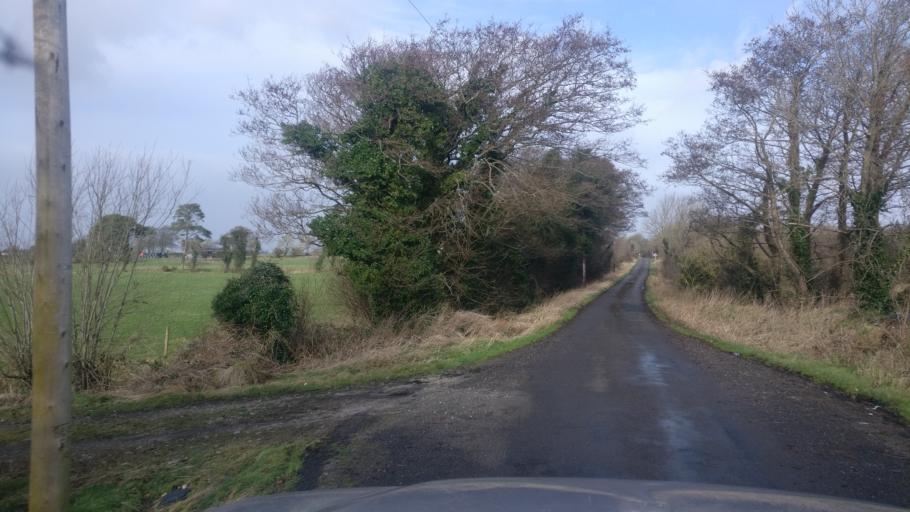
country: IE
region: Connaught
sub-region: County Galway
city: Loughrea
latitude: 53.2742
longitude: -8.5790
